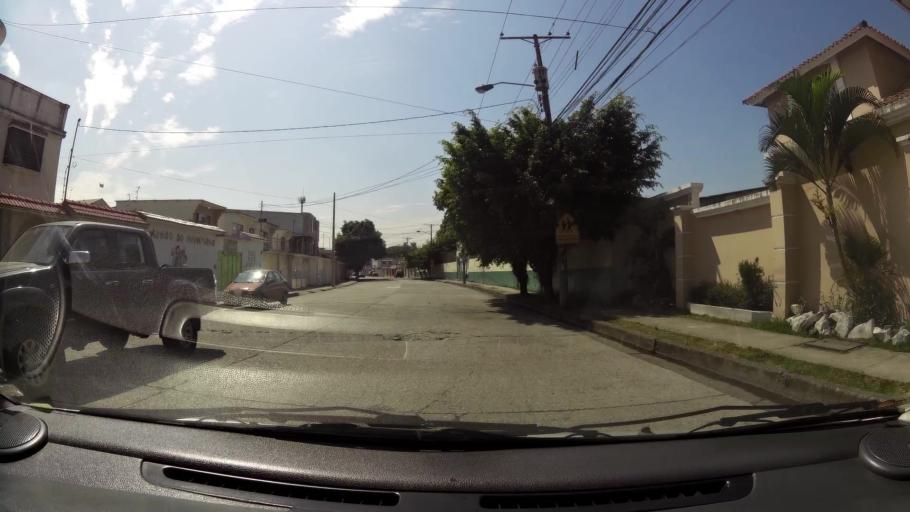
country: EC
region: Guayas
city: Eloy Alfaro
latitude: -2.1349
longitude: -79.9133
